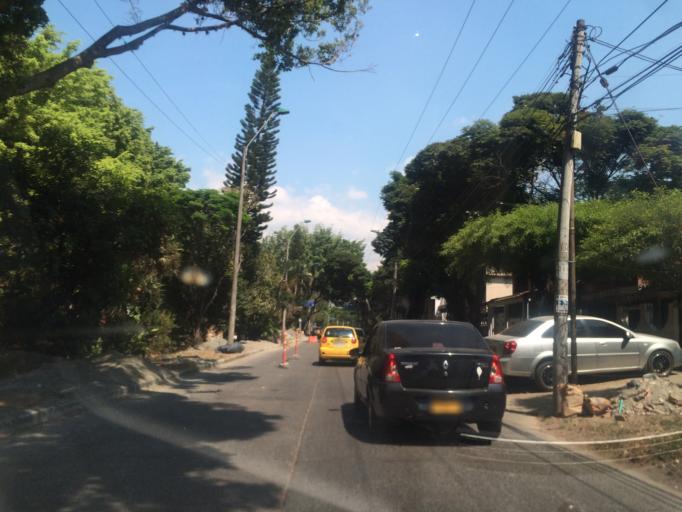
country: CO
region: Valle del Cauca
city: Cali
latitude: 3.4094
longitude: -76.5354
